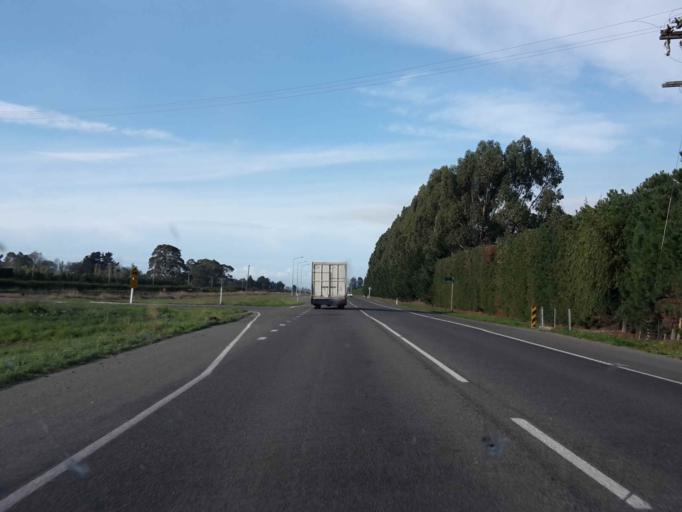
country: NZ
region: Canterbury
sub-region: Ashburton District
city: Tinwald
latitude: -43.9335
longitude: 171.6955
